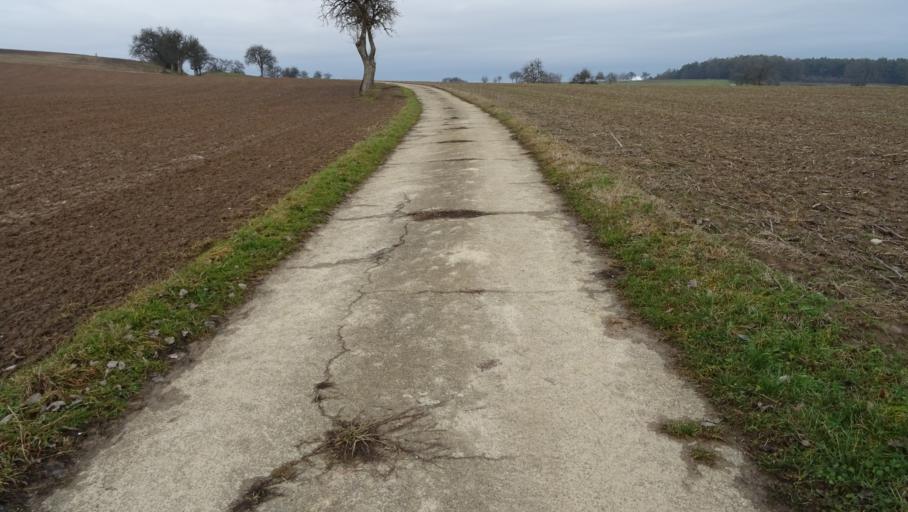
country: DE
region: Baden-Wuerttemberg
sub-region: Karlsruhe Region
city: Mosbach
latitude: 49.3615
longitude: 9.1812
